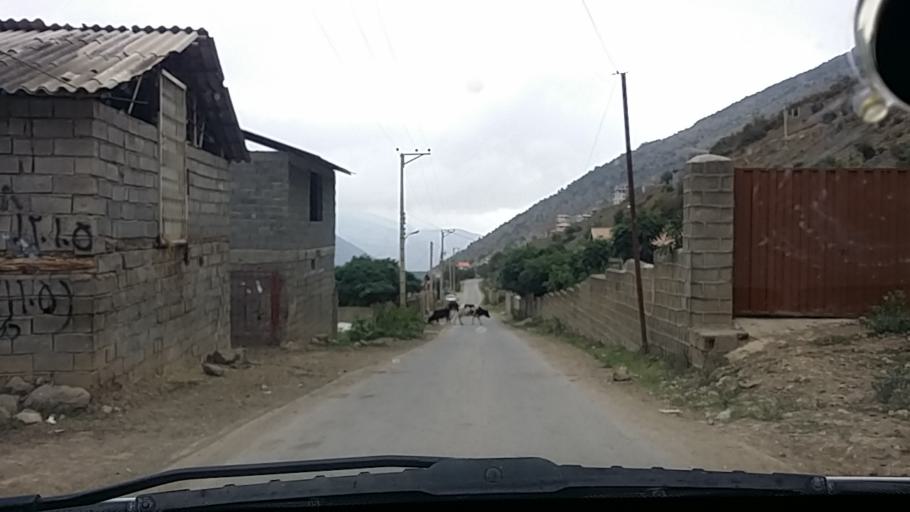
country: IR
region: Mazandaran
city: `Abbasabad
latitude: 36.4689
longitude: 51.1396
